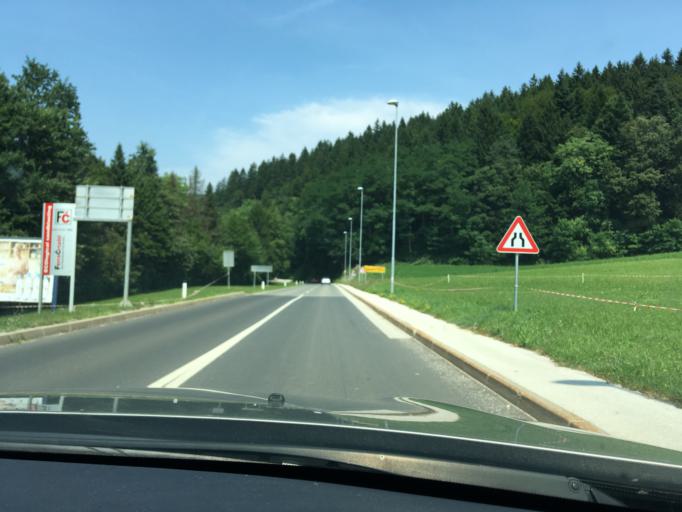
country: SI
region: Dolenjske Toplice
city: Dolenjske Toplice
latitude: 45.7606
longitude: 15.0571
